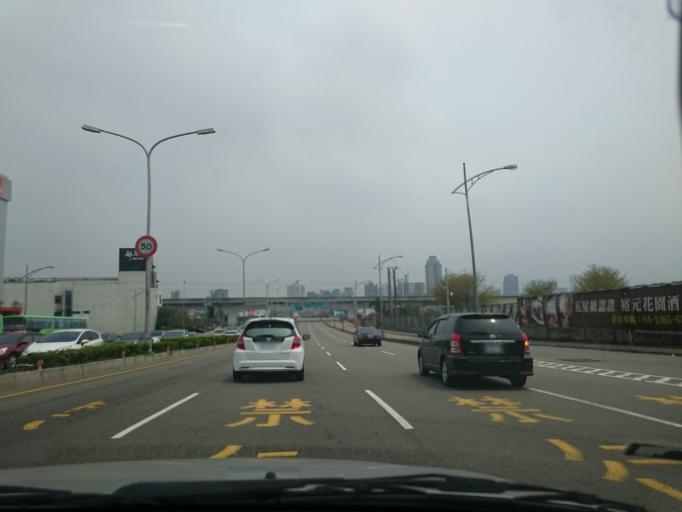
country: TW
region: Taiwan
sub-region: Taichung City
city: Taichung
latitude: 24.1784
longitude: 120.6246
